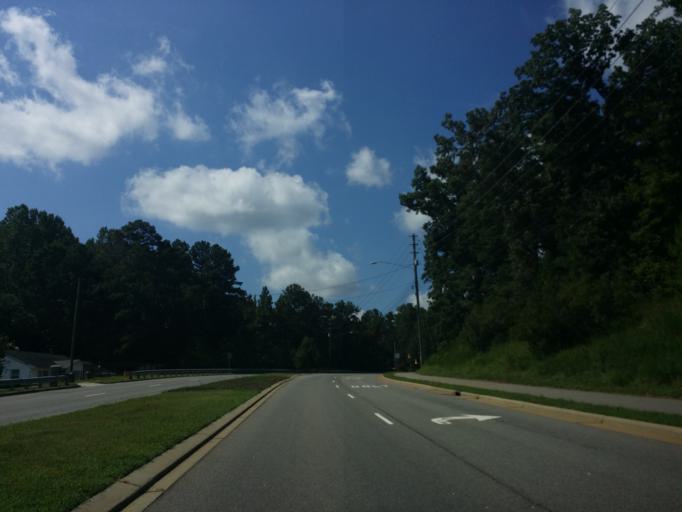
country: US
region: North Carolina
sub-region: Wake County
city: West Raleigh
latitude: 35.8702
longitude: -78.7001
